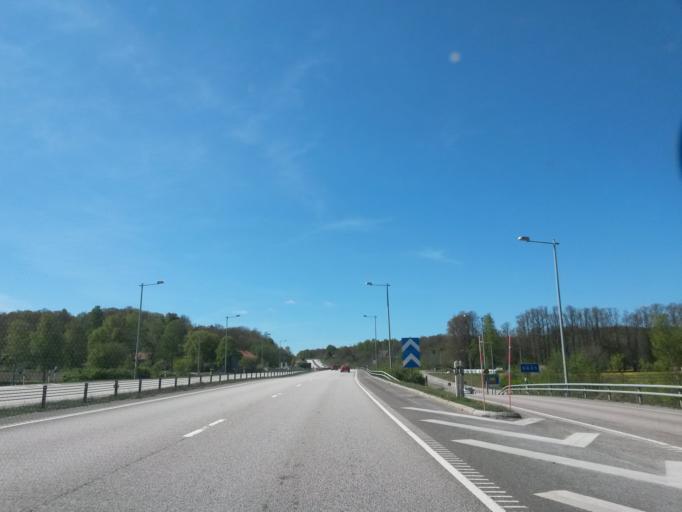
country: SE
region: Vaestra Goetaland
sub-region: Alingsas Kommun
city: Ingared
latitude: 57.8103
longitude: 12.3989
